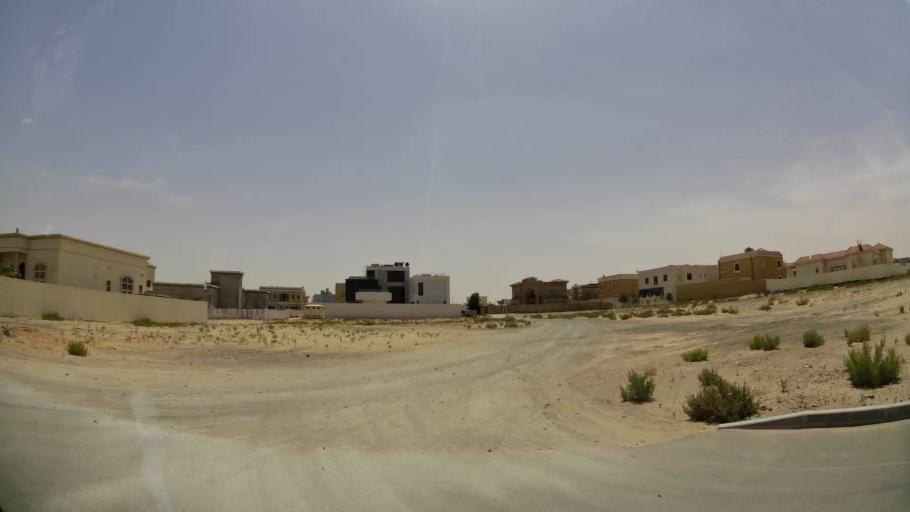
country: AE
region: Ash Shariqah
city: Sharjah
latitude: 25.1923
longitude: 55.4194
